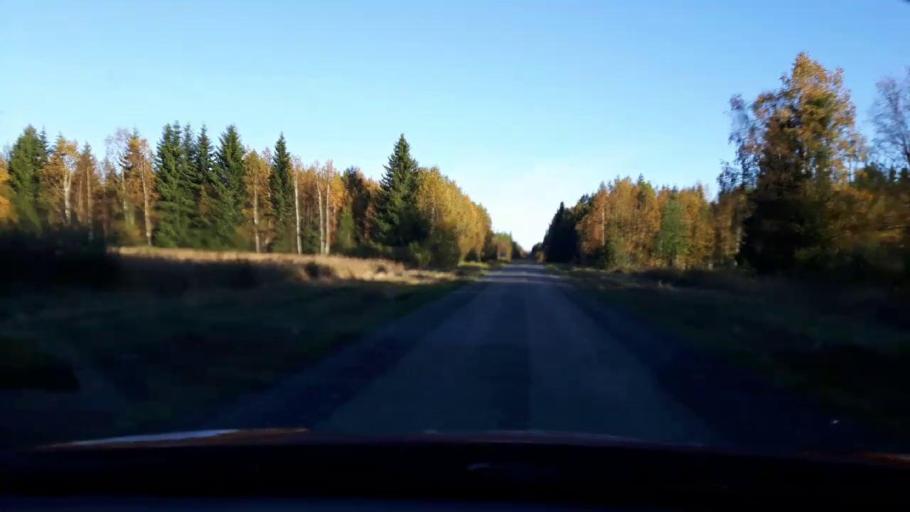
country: SE
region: Jaemtland
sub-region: OEstersunds Kommun
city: Lit
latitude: 63.6039
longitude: 14.7985
